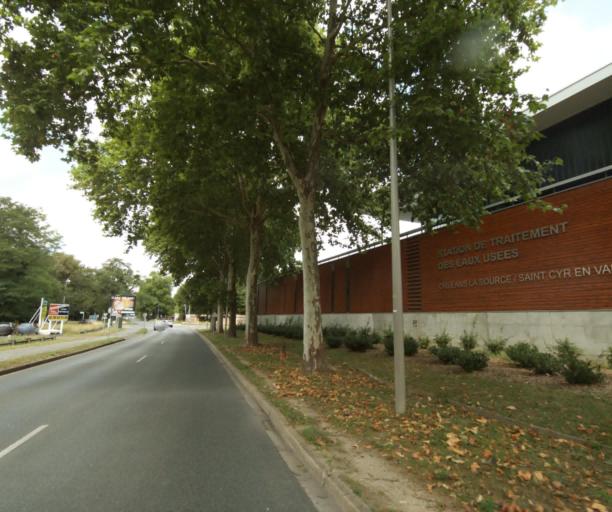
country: FR
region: Centre
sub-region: Departement du Loiret
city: Saint-Cyr-en-Val
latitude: 47.8458
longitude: 1.9421
